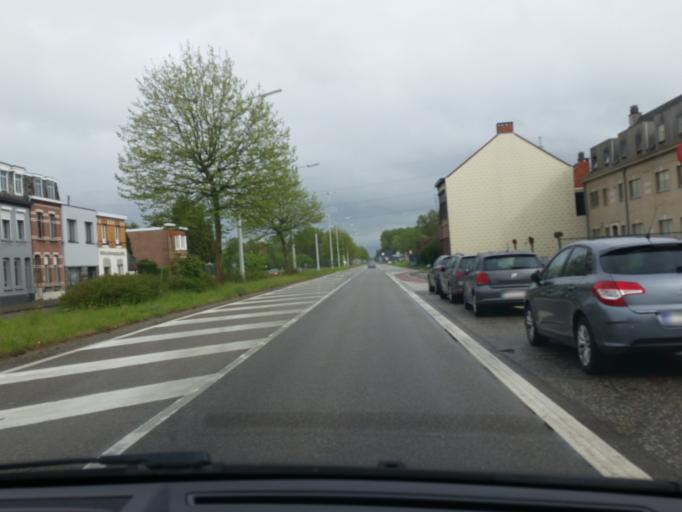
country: BE
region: Flanders
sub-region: Provincie Antwerpen
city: Boechout
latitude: 51.1543
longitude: 4.5226
